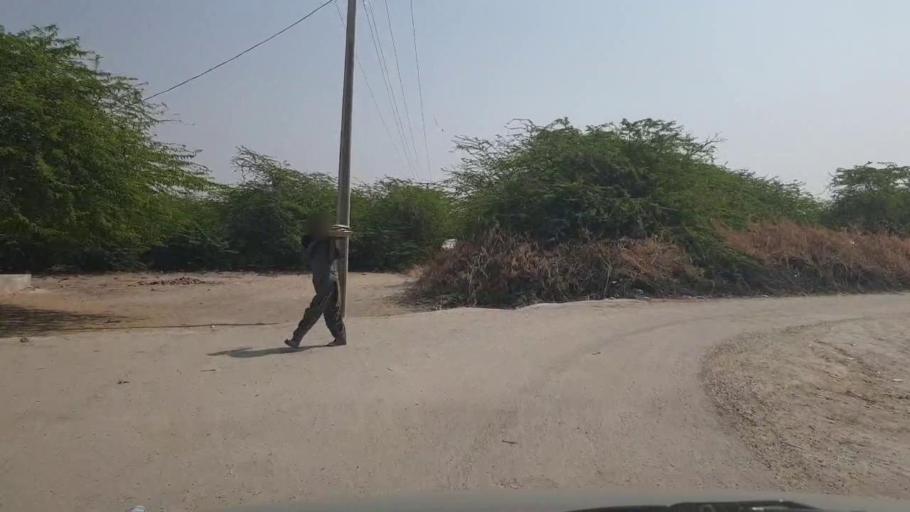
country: PK
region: Sindh
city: Chor
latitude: 25.4880
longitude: 69.7828
